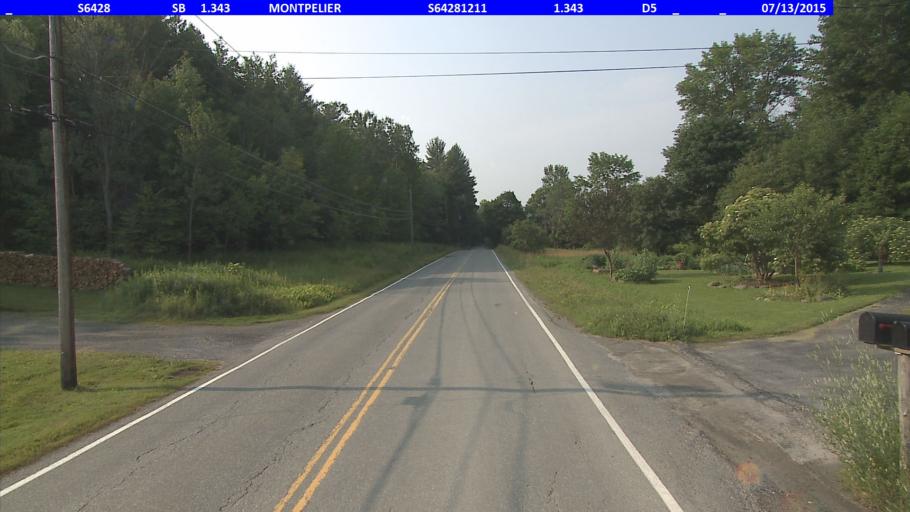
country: US
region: Vermont
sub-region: Washington County
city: Montpelier
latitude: 44.2805
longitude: -72.5936
